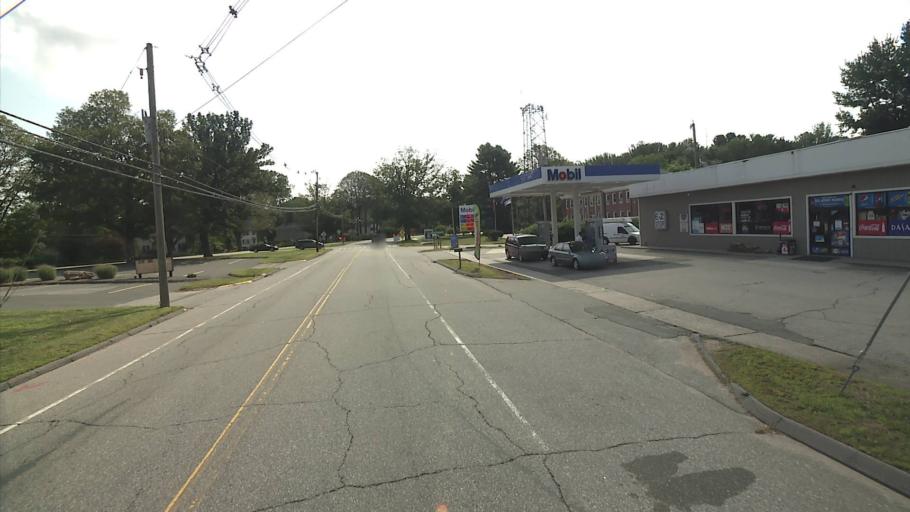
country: US
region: Connecticut
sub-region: New London County
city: Colchester
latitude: 41.5794
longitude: -72.3399
